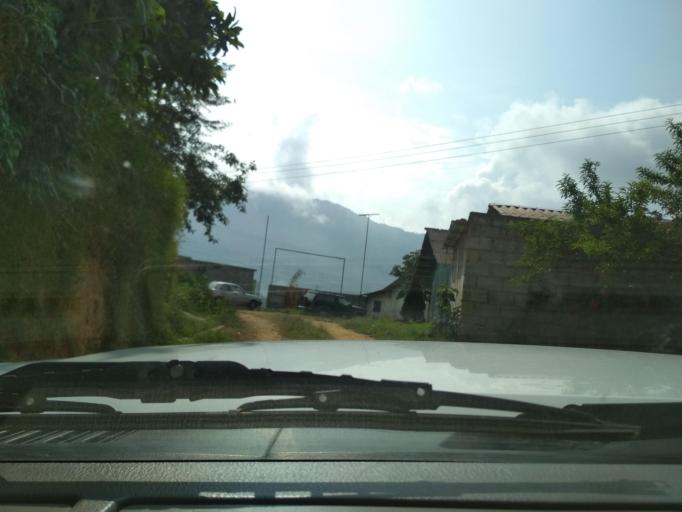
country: MX
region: Veracruz
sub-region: Soledad Atzompa
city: Tlatilpa
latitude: 18.7549
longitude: -97.1505
